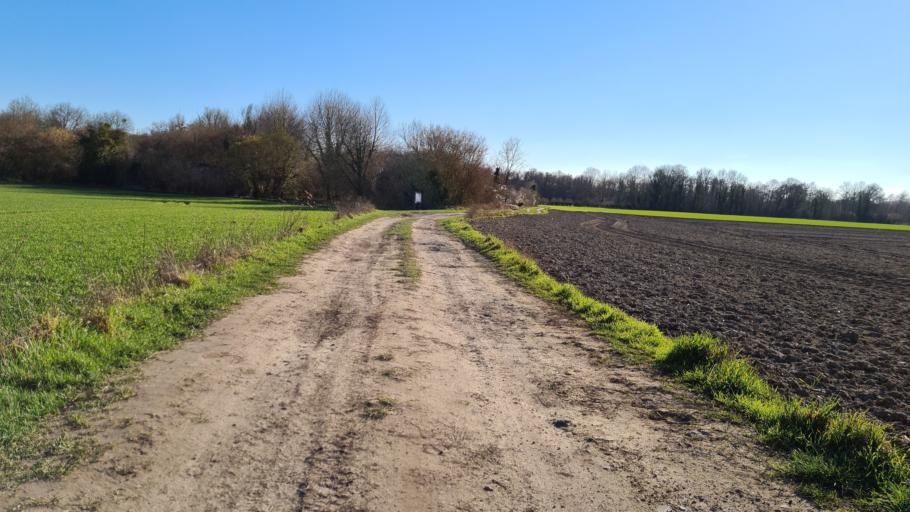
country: FR
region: Picardie
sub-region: Departement de l'Aisne
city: Bruyeres-et-Montberault
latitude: 49.5558
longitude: 3.6556
